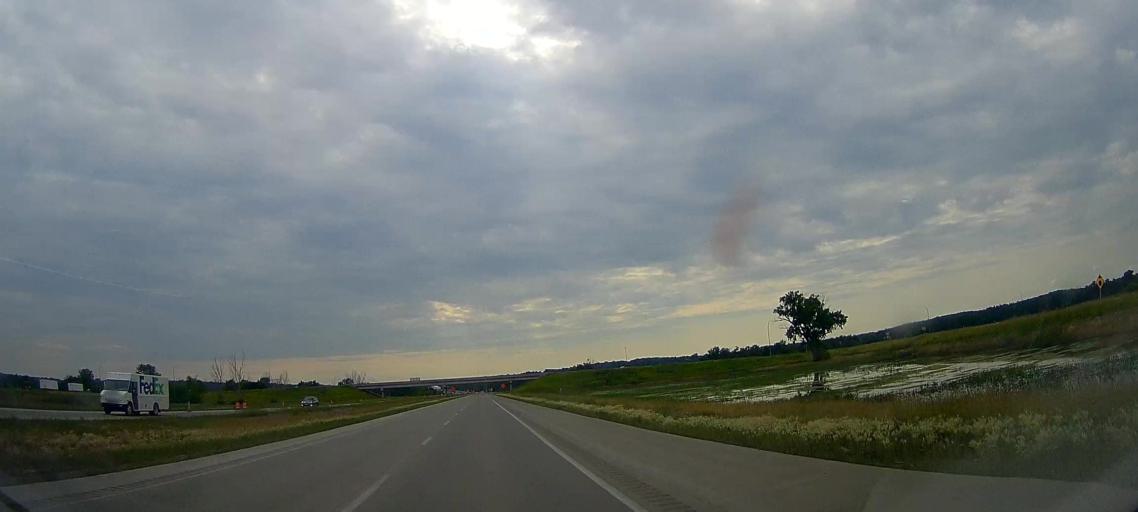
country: US
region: Iowa
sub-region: Pottawattamie County
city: Carter Lake
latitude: 41.3466
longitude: -95.9328
